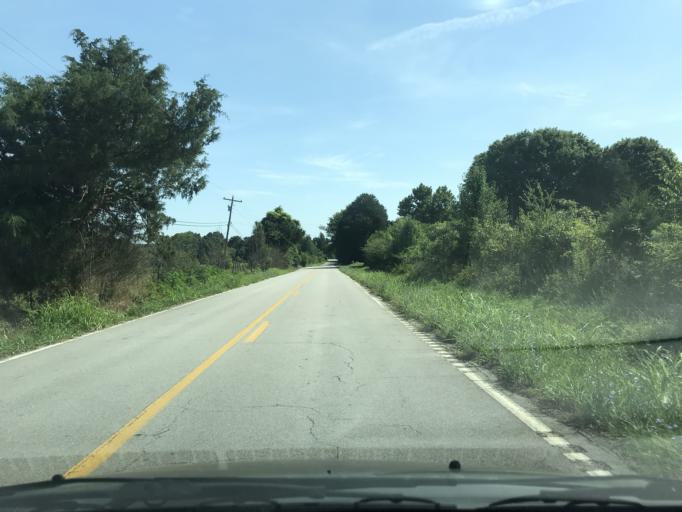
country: US
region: Tennessee
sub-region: Hamilton County
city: Sale Creek
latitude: 35.3243
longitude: -85.0187
